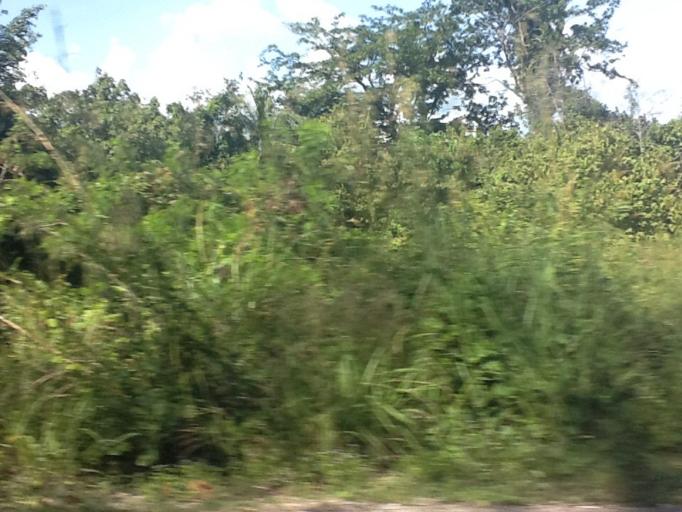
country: TH
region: Phuket
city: Thalang
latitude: 8.1203
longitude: 98.3344
